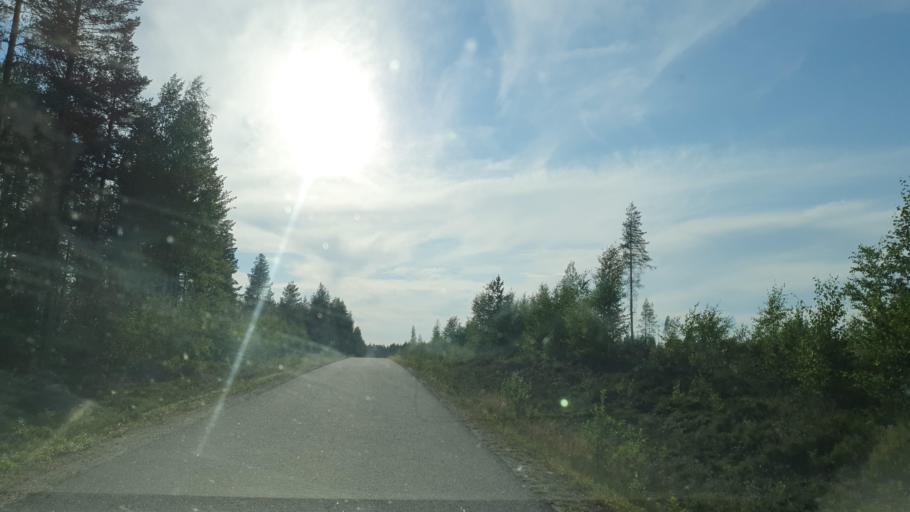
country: FI
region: Kainuu
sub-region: Kehys-Kainuu
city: Kuhmo
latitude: 64.2812
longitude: 29.4088
